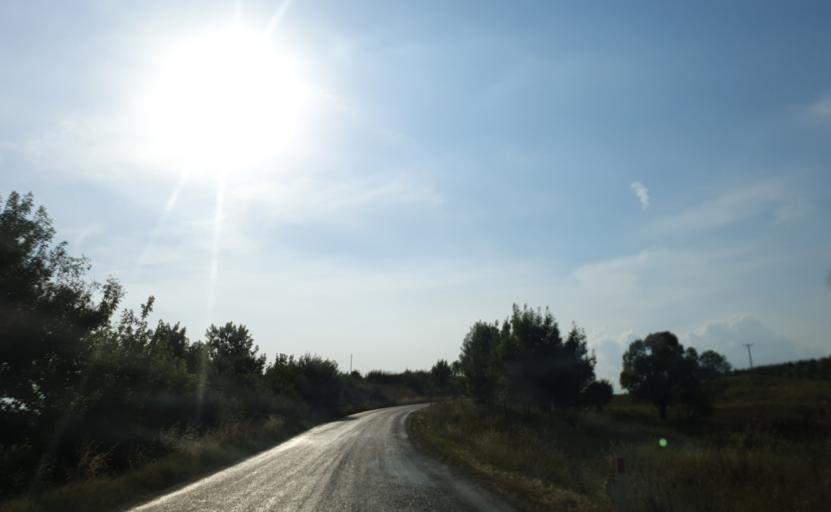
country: TR
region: Tekirdag
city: Muratli
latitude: 41.2034
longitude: 27.4657
